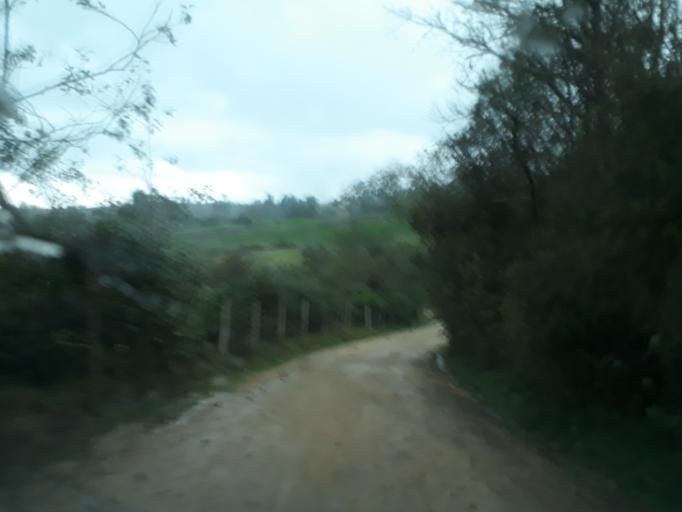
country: CO
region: Cundinamarca
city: Villapinzon
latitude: 5.2947
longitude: -73.6158
